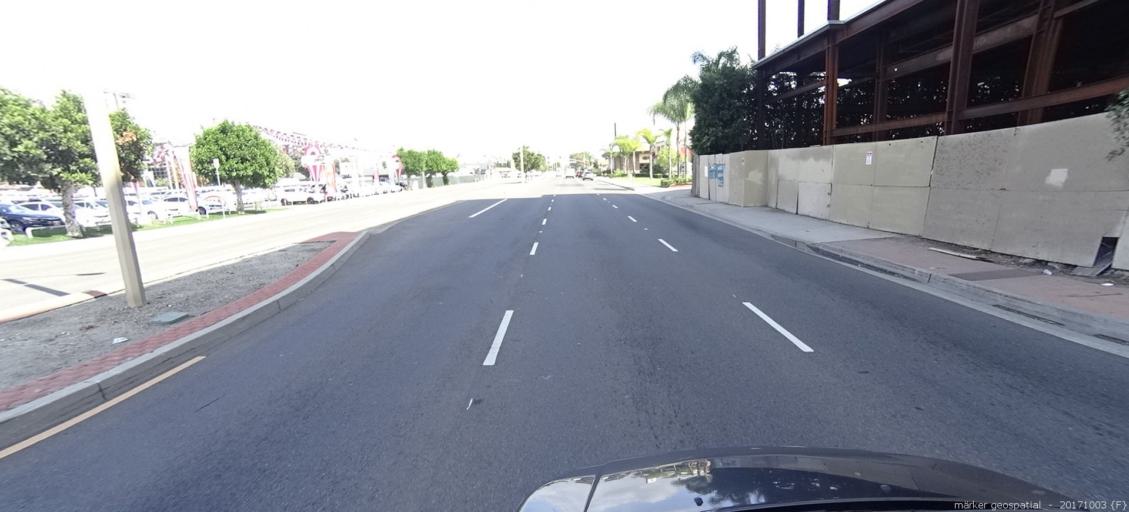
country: US
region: California
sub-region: Orange County
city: Garden Grove
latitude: 33.7740
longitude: -117.9571
